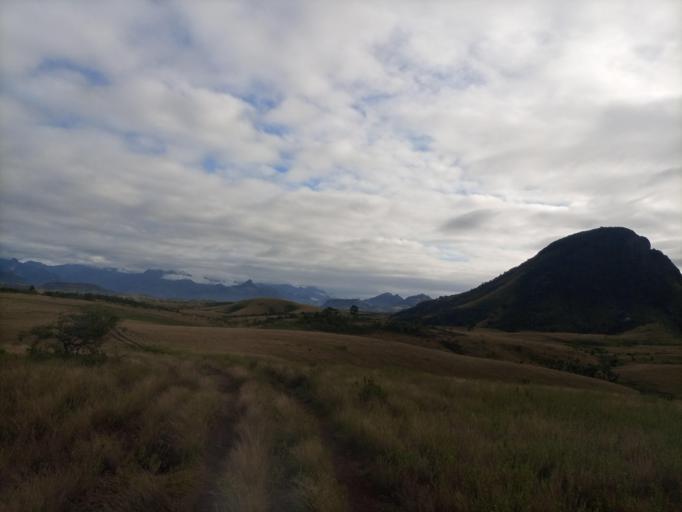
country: MG
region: Anosy
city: Fort Dauphin
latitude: -24.3130
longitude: 47.2519
